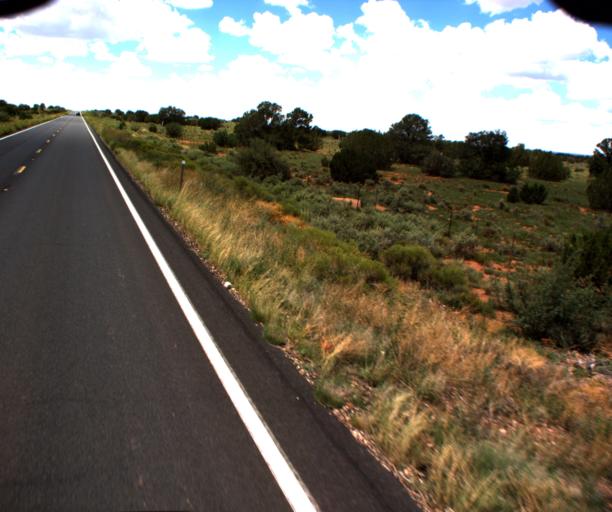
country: US
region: Arizona
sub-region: Coconino County
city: Parks
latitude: 35.6103
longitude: -112.0625
